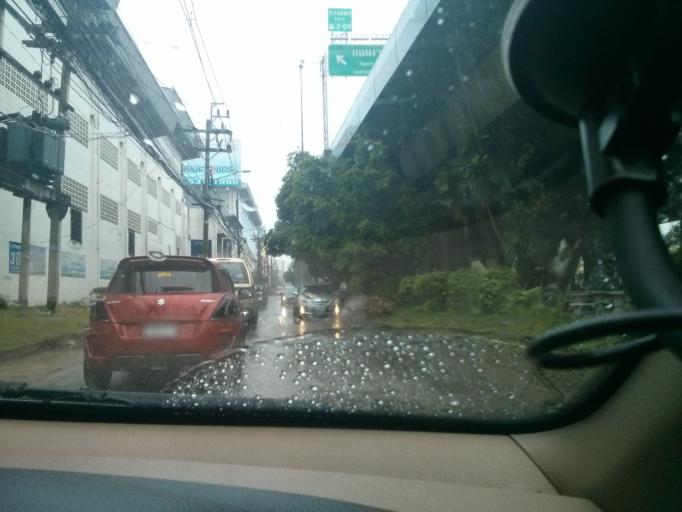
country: TH
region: Nonthaburi
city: Mueang Nonthaburi
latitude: 13.8473
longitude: 100.5330
